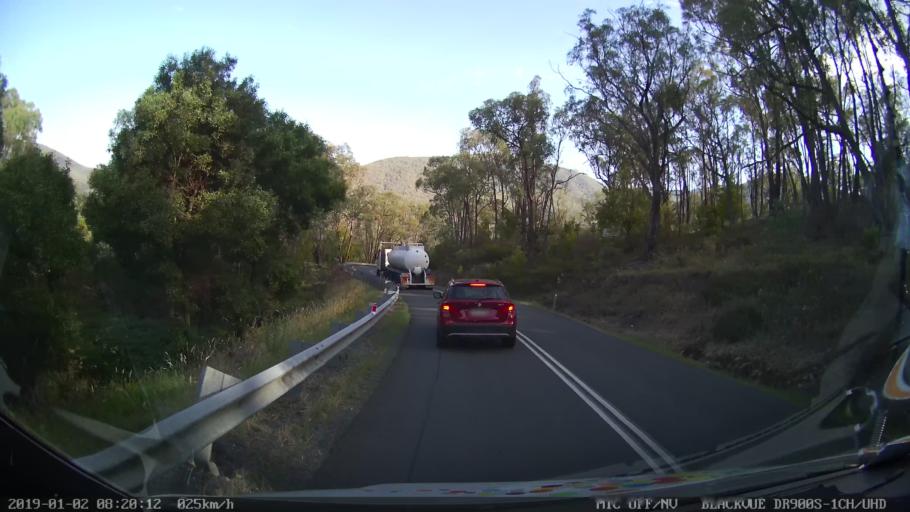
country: AU
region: New South Wales
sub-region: Tumut Shire
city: Tumut
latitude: -35.5733
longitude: 148.3241
